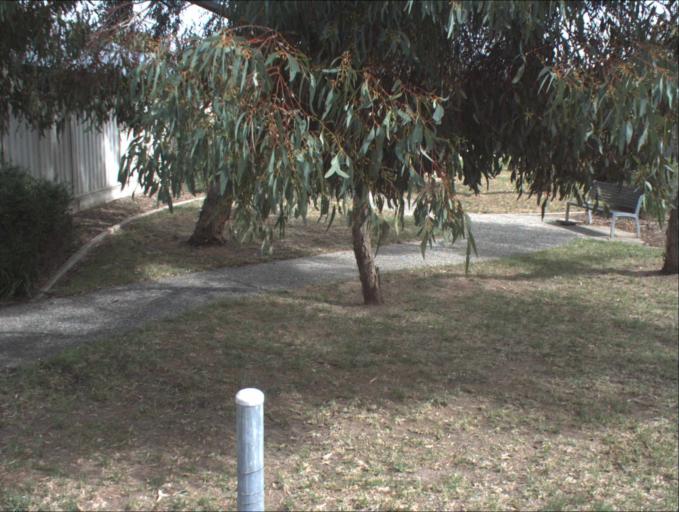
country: AU
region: South Australia
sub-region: Port Adelaide Enfield
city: Blair Athol
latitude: -34.8677
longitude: 138.5918
